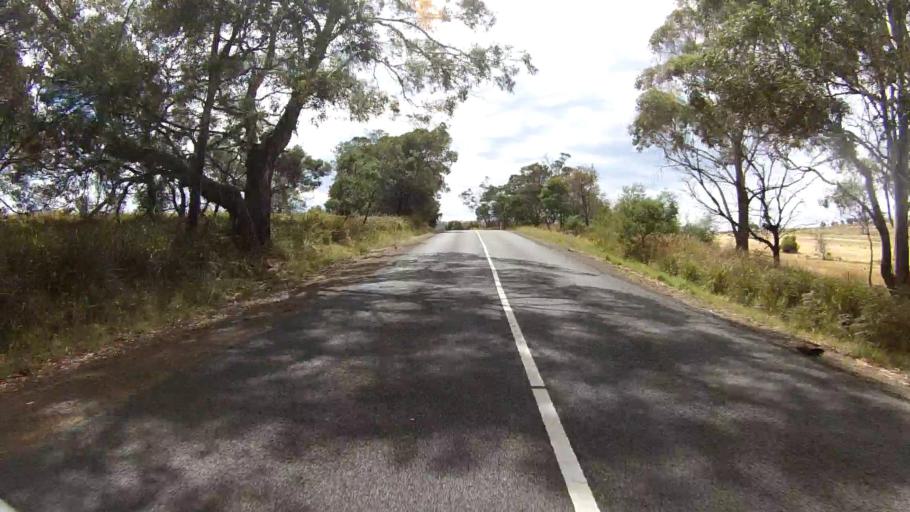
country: AU
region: Tasmania
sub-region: Sorell
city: Sorell
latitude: -42.8758
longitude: 147.6793
